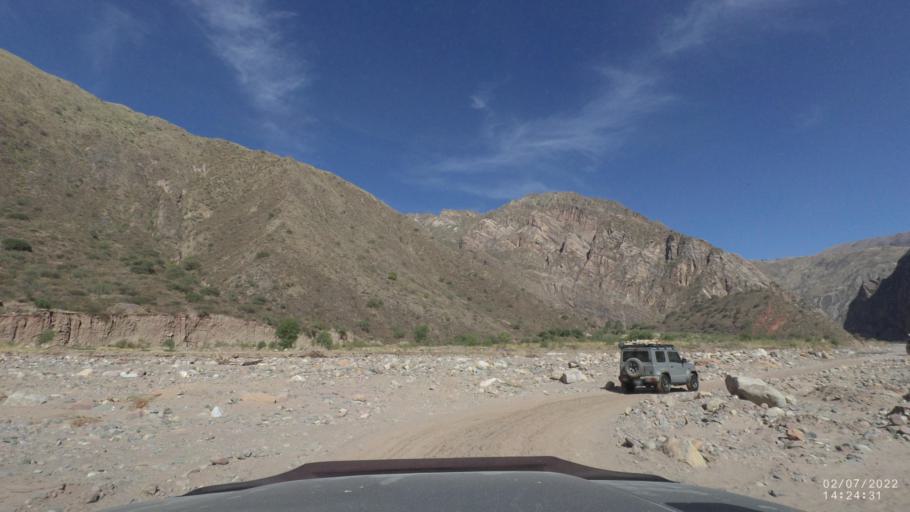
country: BO
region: Cochabamba
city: Irpa Irpa
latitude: -17.8331
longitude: -66.4137
